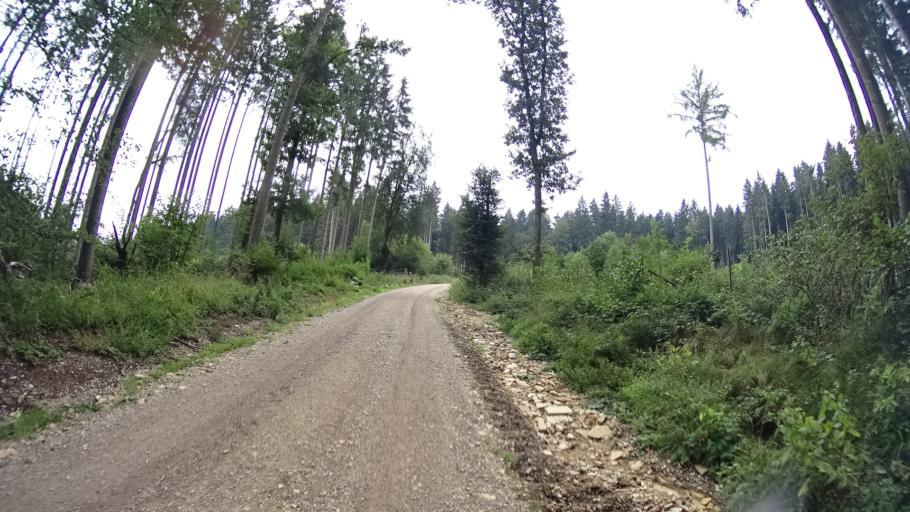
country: DE
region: Bavaria
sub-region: Upper Bavaria
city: Bohmfeld
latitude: 48.8779
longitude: 11.3570
